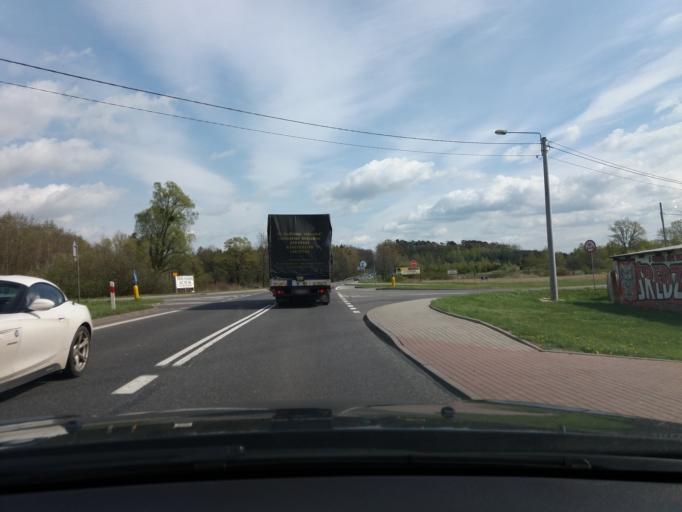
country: PL
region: Lower Silesian Voivodeship
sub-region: Powiat sredzki
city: Malczyce
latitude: 51.1945
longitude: 16.5018
